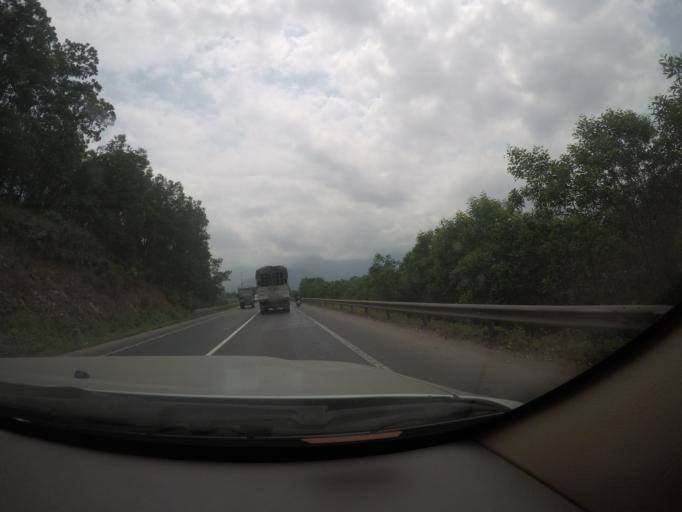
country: VN
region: Thua Thien-Hue
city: Phu Loc
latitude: 16.2747
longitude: 107.9203
